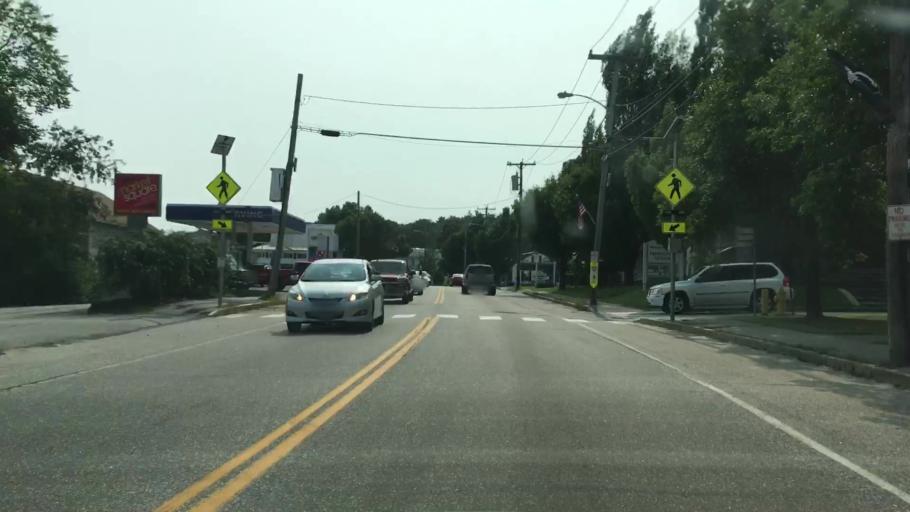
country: US
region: Maine
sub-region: Oxford County
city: South Paris
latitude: 44.2233
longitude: -70.5141
